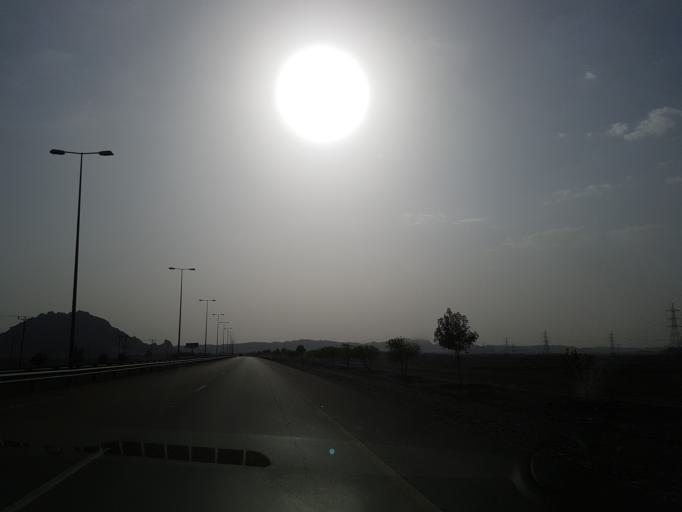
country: OM
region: Al Buraimi
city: Al Buraymi
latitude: 24.2460
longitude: 55.9995
